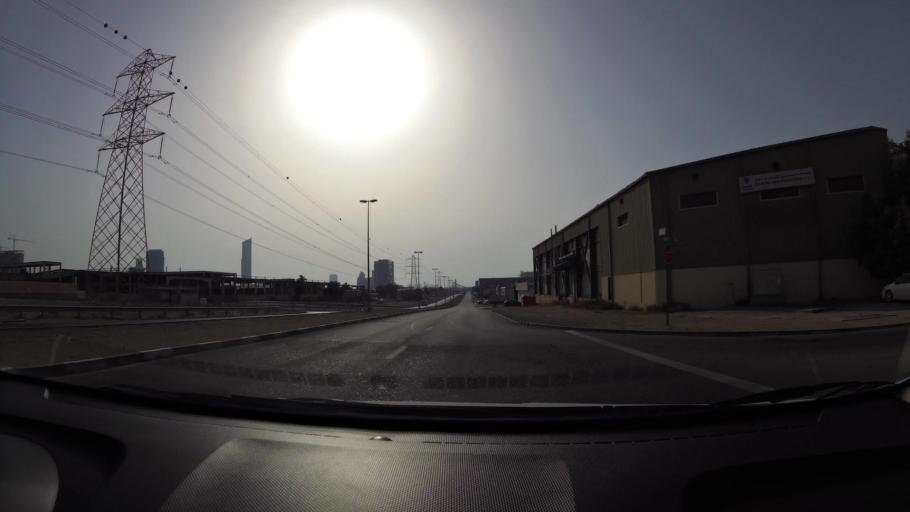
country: AE
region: Ash Shariqah
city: Sharjah
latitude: 25.2270
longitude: 55.3661
